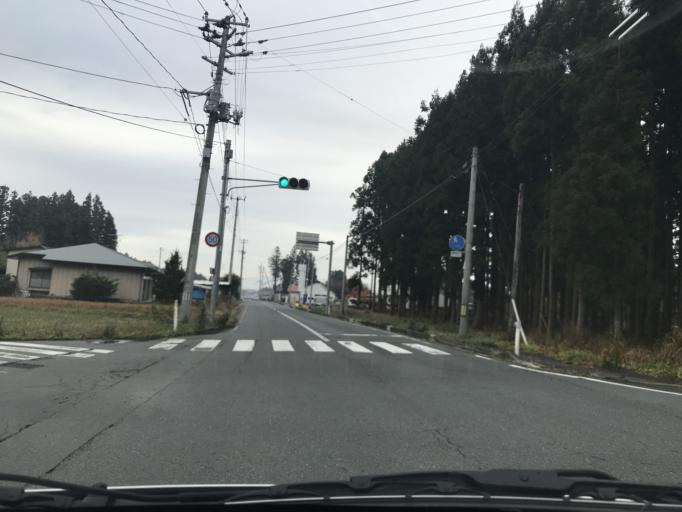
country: JP
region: Iwate
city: Mizusawa
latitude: 39.1054
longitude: 141.1027
